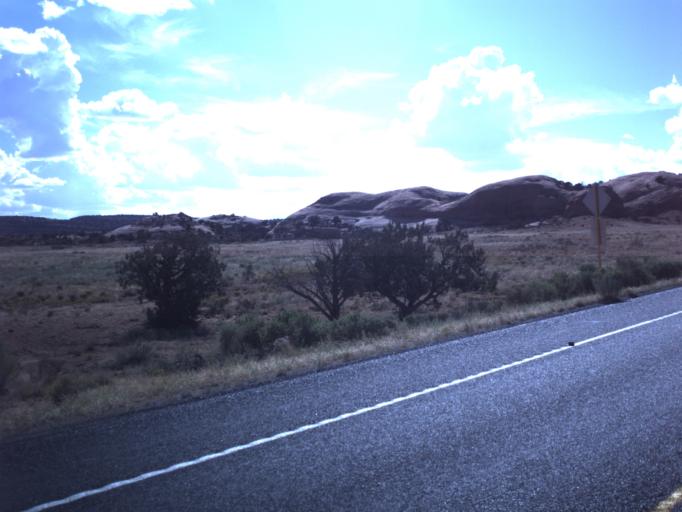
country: US
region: Utah
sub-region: Grand County
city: Moab
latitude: 38.6355
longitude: -109.7785
